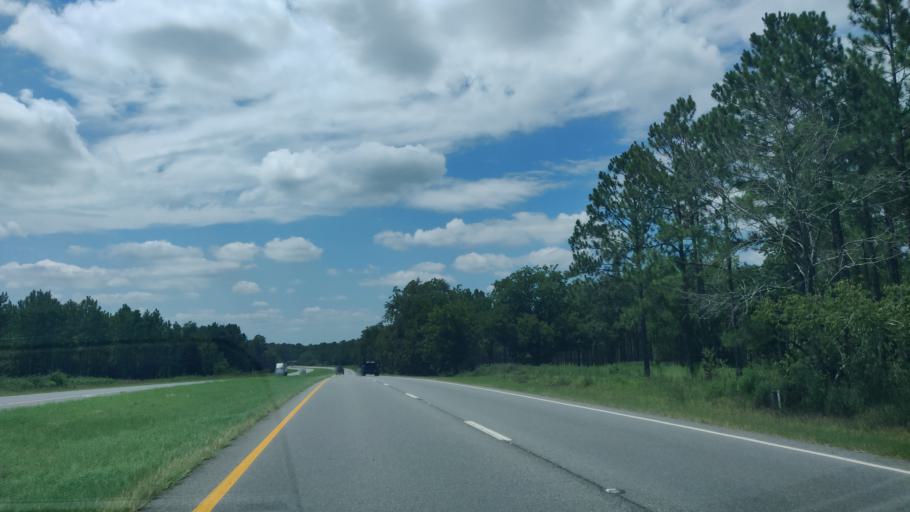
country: US
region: Georgia
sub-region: Tift County
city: Tifton
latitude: 31.4695
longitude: -83.6316
